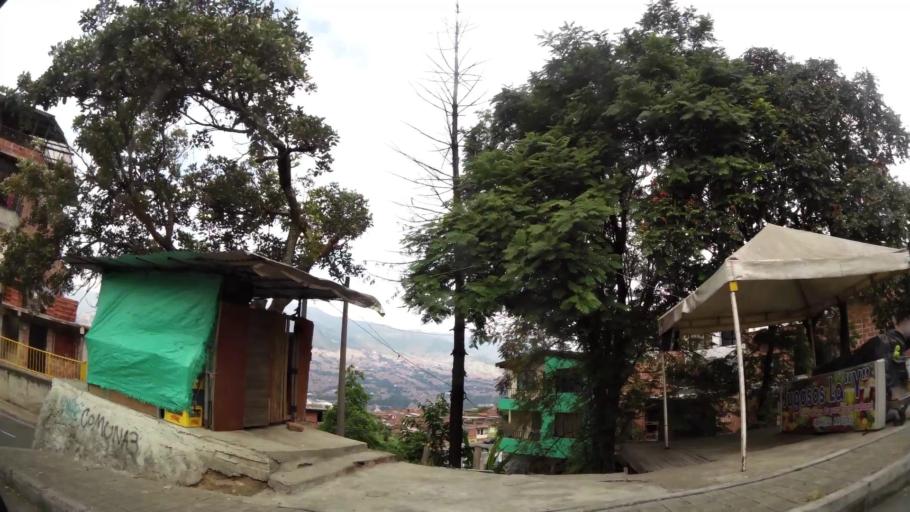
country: CO
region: Antioquia
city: Medellin
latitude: 6.2813
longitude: -75.5515
